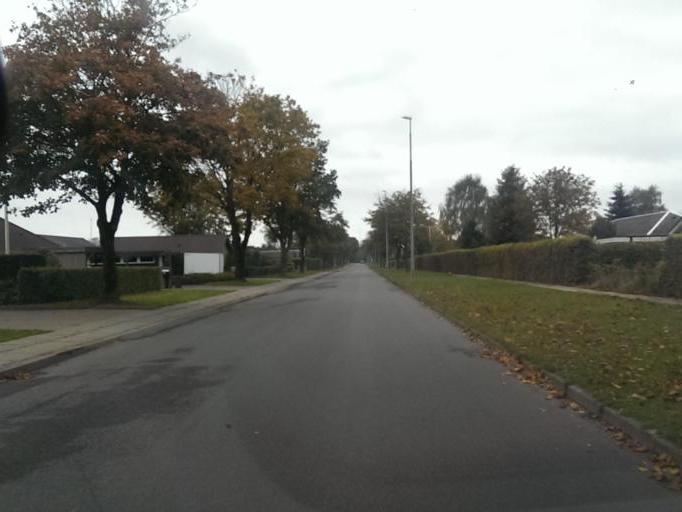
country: DK
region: South Denmark
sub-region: Esbjerg Kommune
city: Bramming
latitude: 55.4663
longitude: 8.7150
